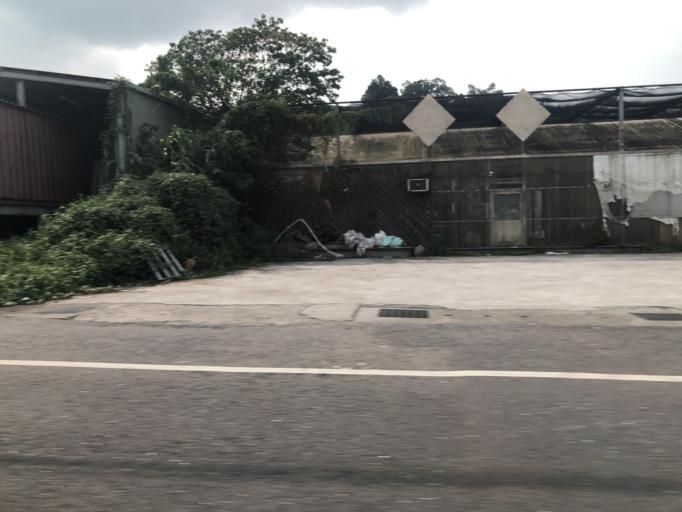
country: TW
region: Taiwan
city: Daxi
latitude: 24.9045
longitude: 121.3571
